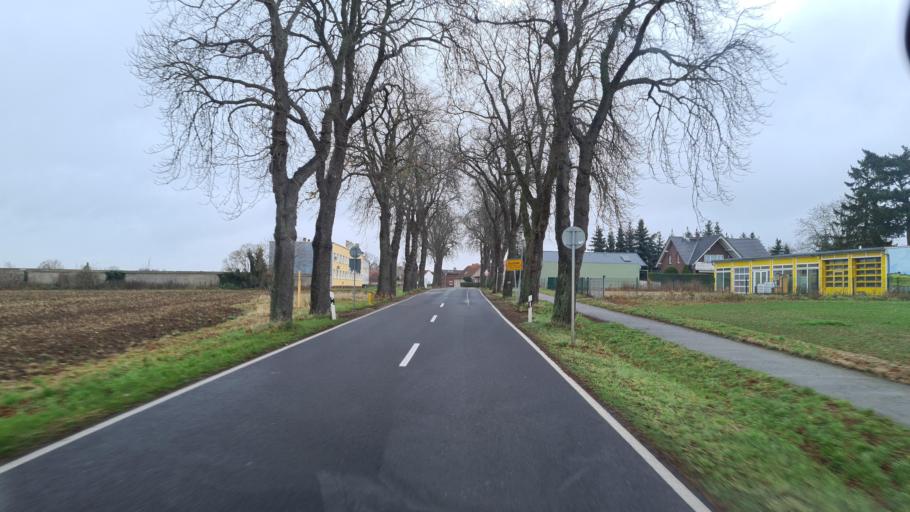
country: DE
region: Brandenburg
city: Retzow
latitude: 52.5832
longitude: 12.6313
